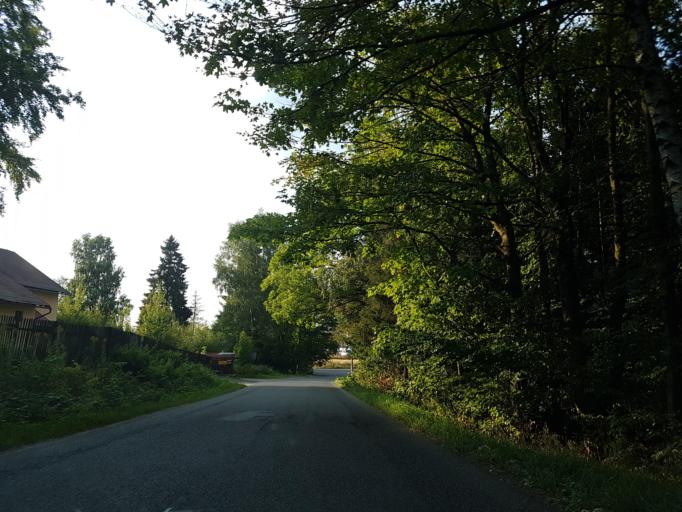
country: CZ
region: Liberecky
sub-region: Okres Jablonec nad Nisou
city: Jablonec nad Nisou
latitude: 50.7152
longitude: 15.1883
